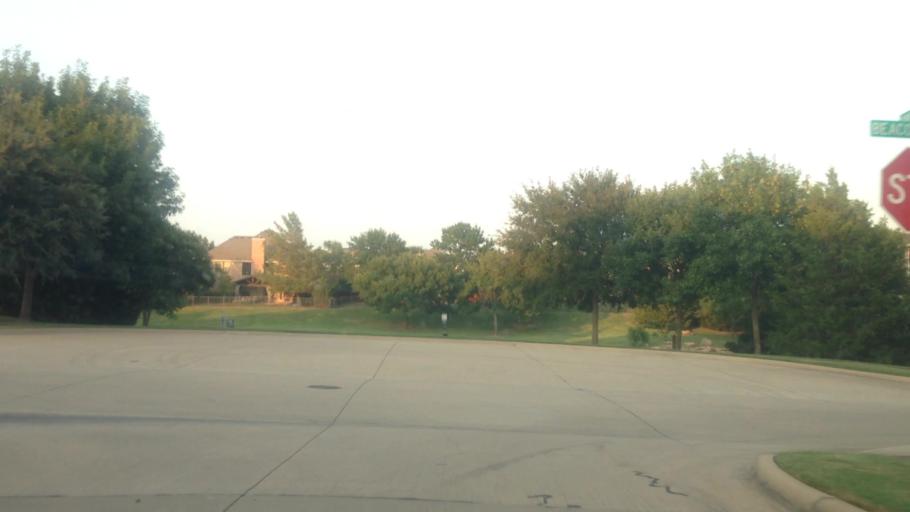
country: US
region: Texas
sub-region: Denton County
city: The Colony
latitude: 33.1247
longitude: -96.8795
